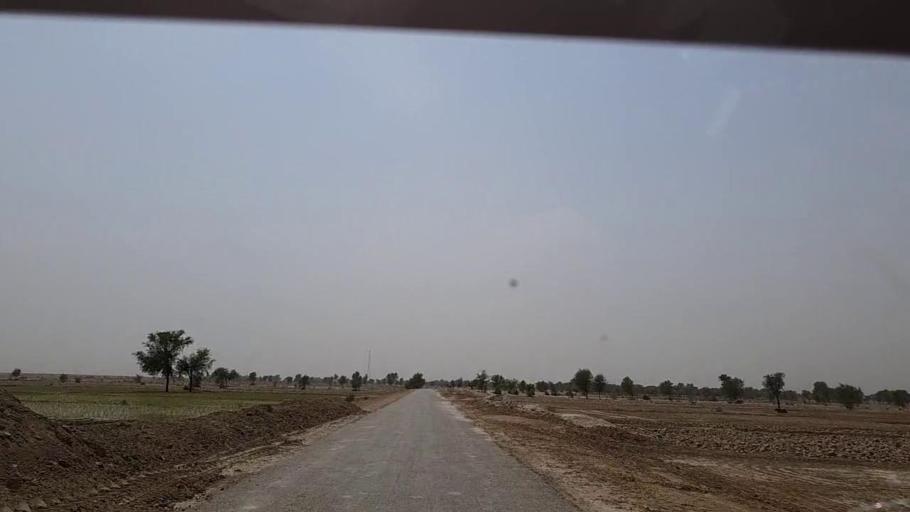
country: PK
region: Sindh
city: Khairpur Nathan Shah
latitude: 27.0166
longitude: 67.6006
